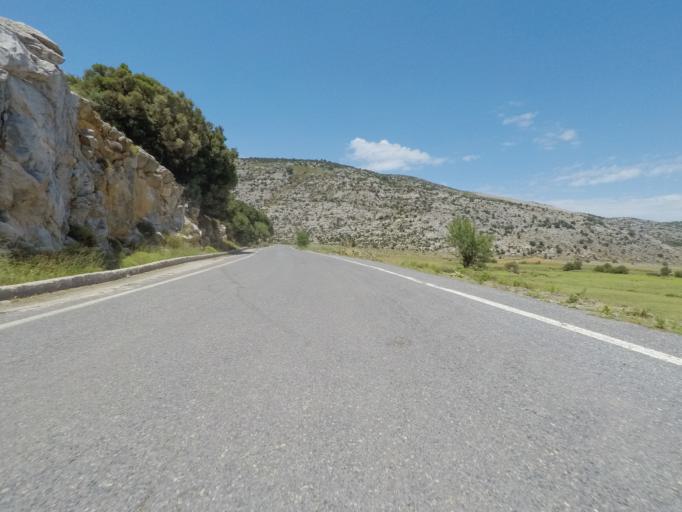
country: GR
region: Crete
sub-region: Nomos Irakleiou
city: Mokhos
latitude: 35.1901
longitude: 25.4322
